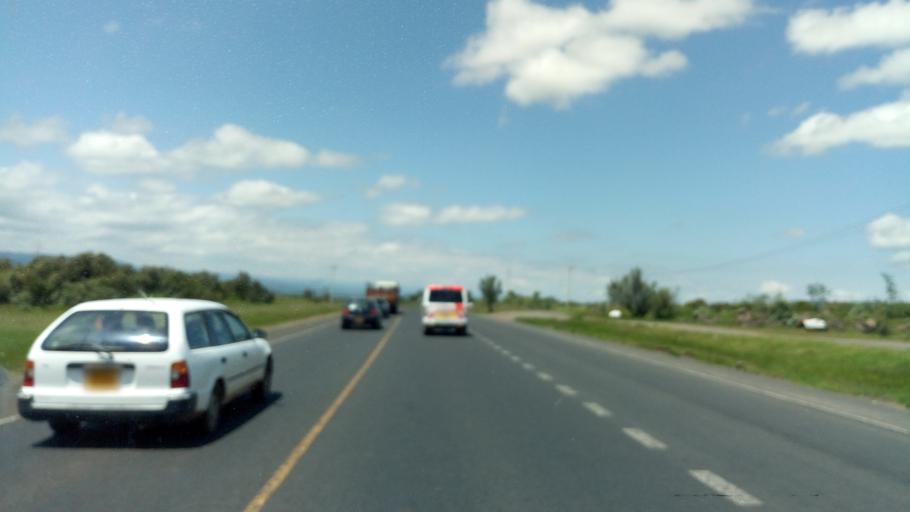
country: KE
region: Nakuru
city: Naivasha
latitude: -0.5387
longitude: 36.3361
